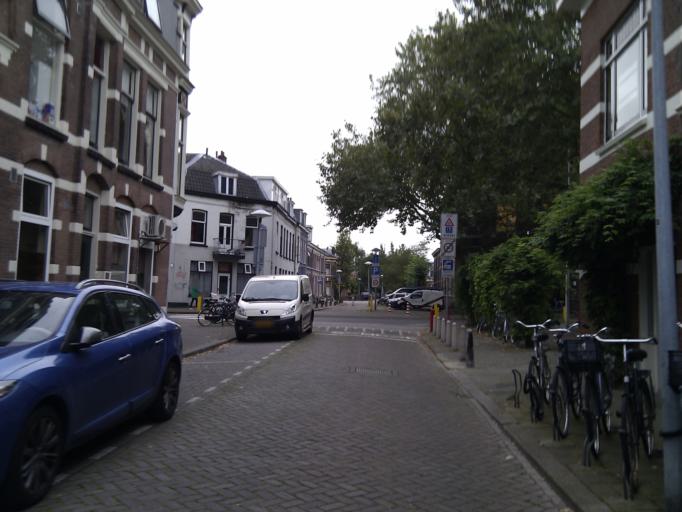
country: NL
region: Utrecht
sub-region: Gemeente Utrecht
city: Utrecht
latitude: 52.0988
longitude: 5.1352
